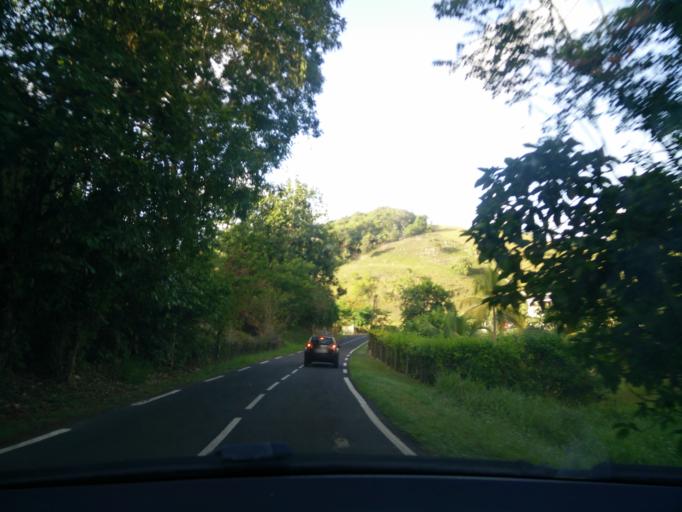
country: GP
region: Guadeloupe
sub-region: Guadeloupe
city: Sainte-Anne
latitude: 16.2782
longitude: -61.4172
